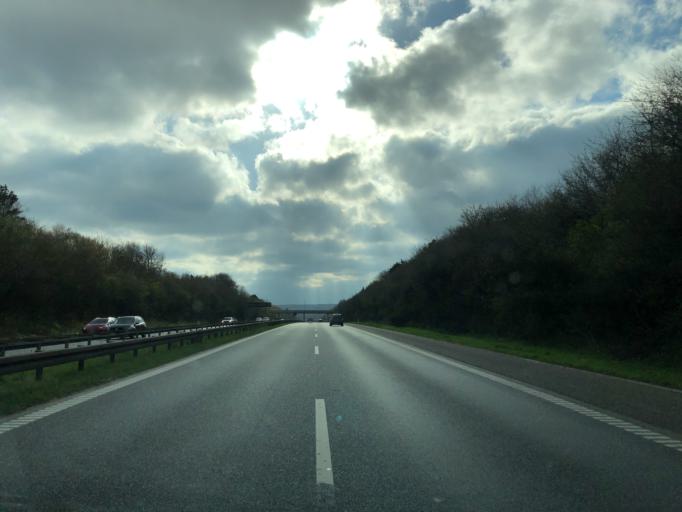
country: DK
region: North Denmark
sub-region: Alborg Kommune
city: Aalborg
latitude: 57.0142
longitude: 9.9427
